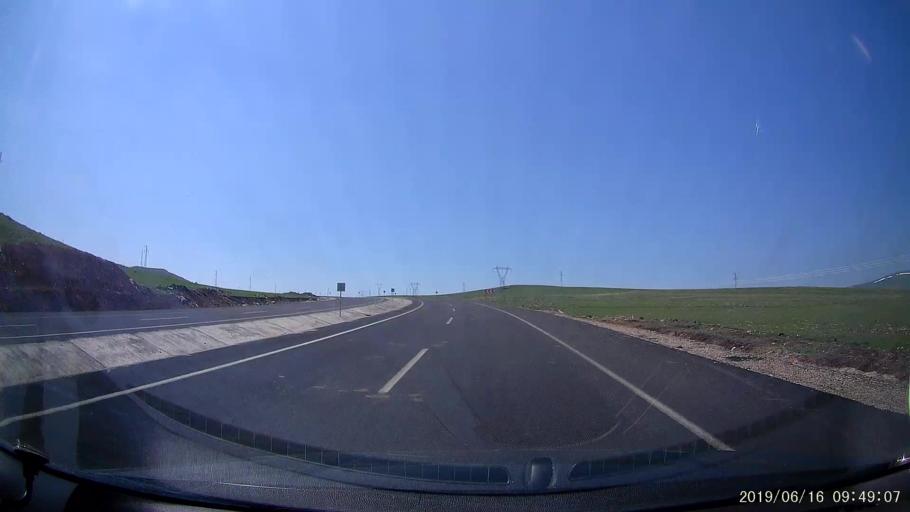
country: TR
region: Kars
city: Digor
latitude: 40.4253
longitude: 43.3564
